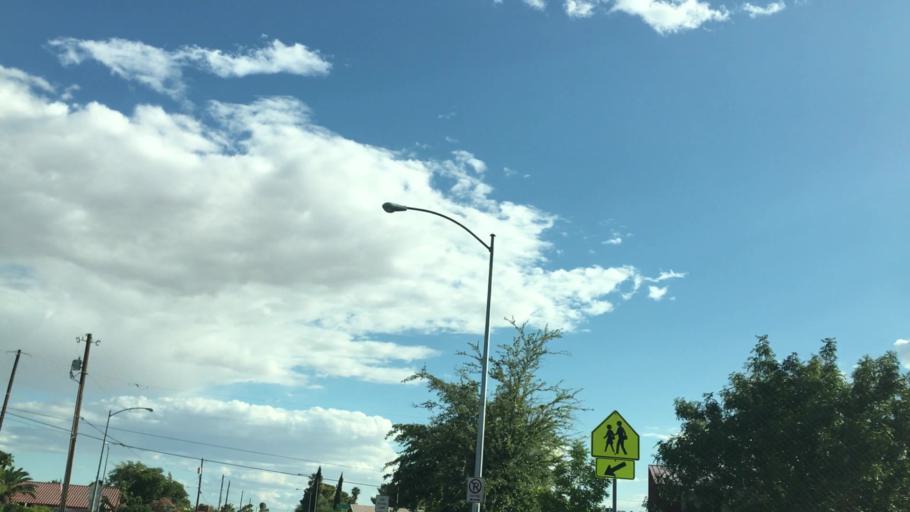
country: US
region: Nevada
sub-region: Clark County
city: Spring Valley
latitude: 36.1300
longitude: -115.2229
